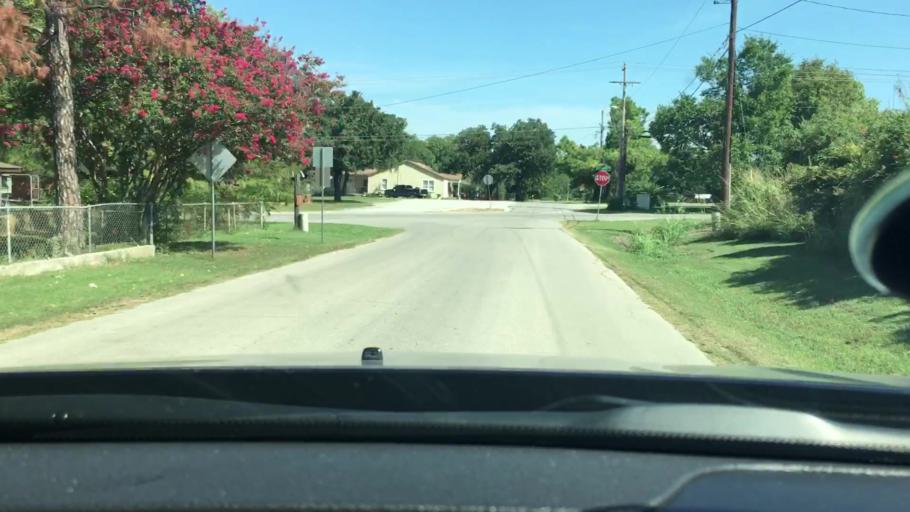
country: US
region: Oklahoma
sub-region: Carter County
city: Ardmore
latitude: 34.1577
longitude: -97.0906
